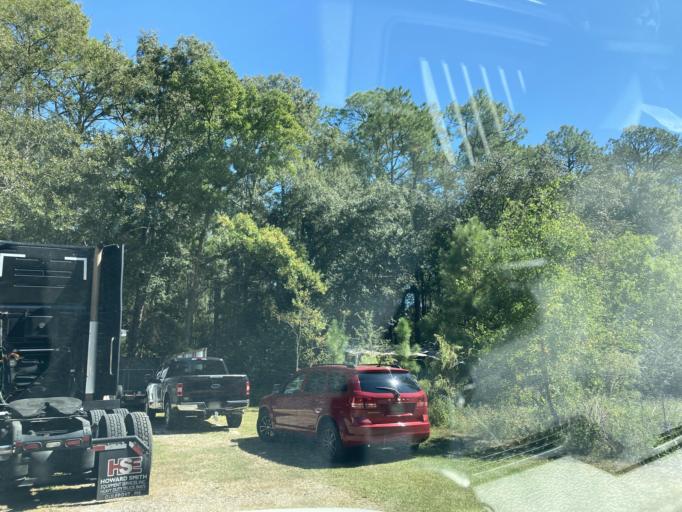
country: US
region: Mississippi
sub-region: Jackson County
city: Saint Martin
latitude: 30.4604
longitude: -88.8754
